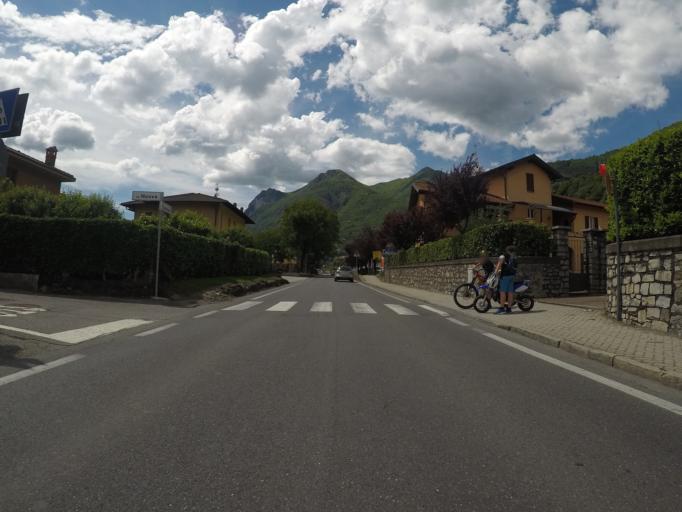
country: IT
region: Lombardy
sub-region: Provincia di Como
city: Corrido
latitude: 46.0403
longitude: 9.1433
